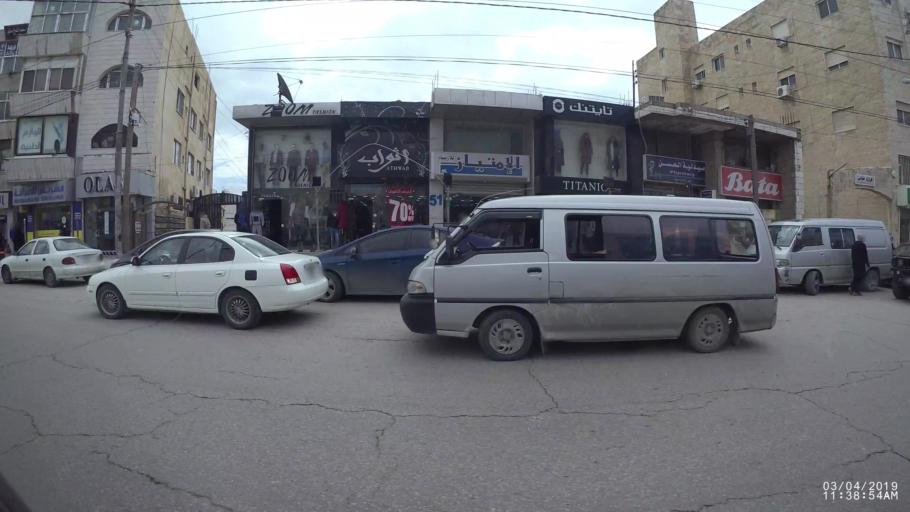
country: JO
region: Amman
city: Wadi as Sir
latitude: 31.9542
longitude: 35.8389
